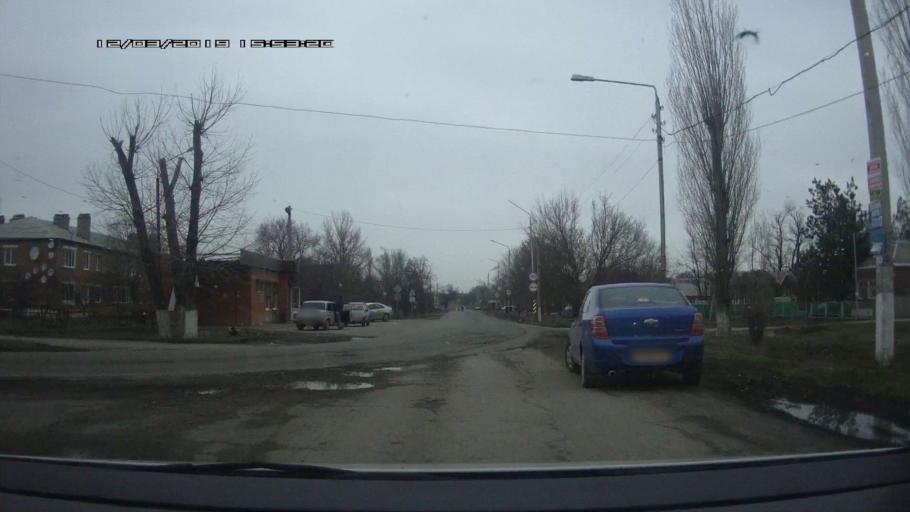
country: RU
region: Rostov
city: Novobataysk
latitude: 46.8847
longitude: 39.7761
